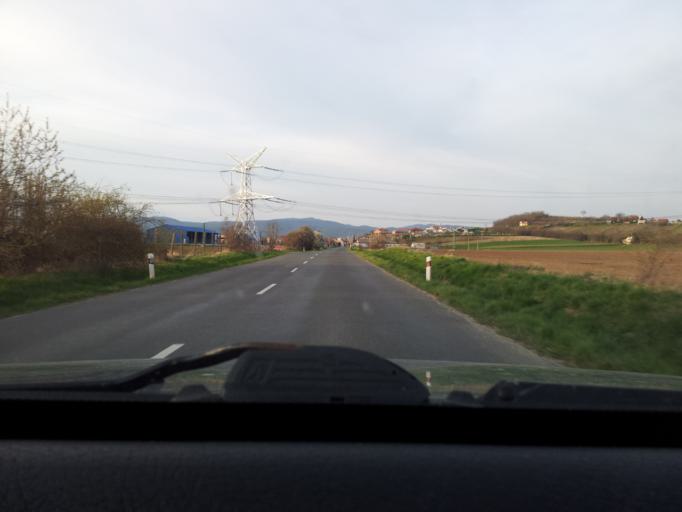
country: SK
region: Nitriansky
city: Levice
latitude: 48.2438
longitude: 18.6004
